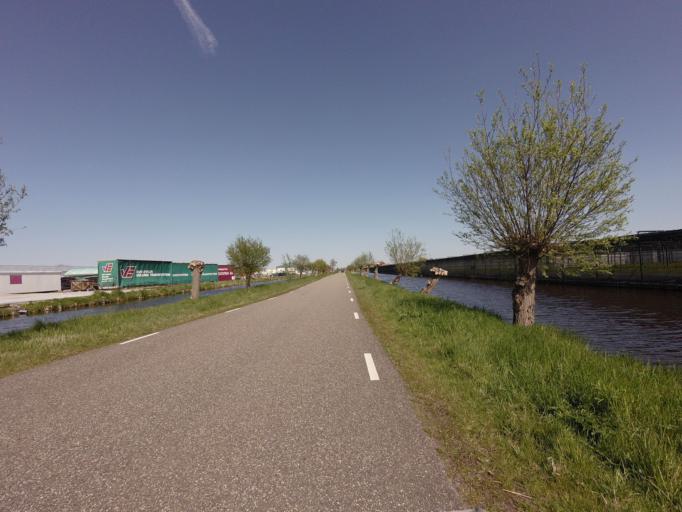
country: NL
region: South Holland
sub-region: Gemeente Boskoop
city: Boskoop
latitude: 52.0964
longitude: 4.6581
